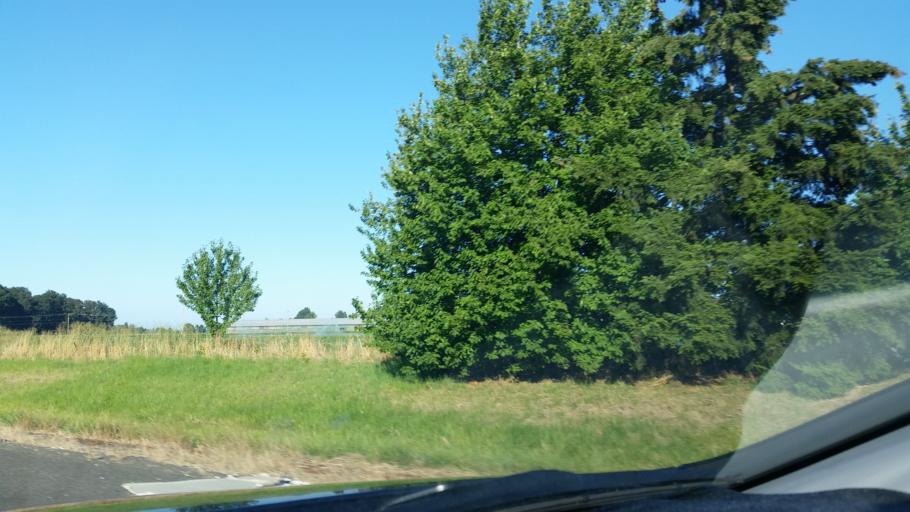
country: US
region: Oregon
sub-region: Clackamas County
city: Wilsonville
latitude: 45.2620
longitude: -122.7842
